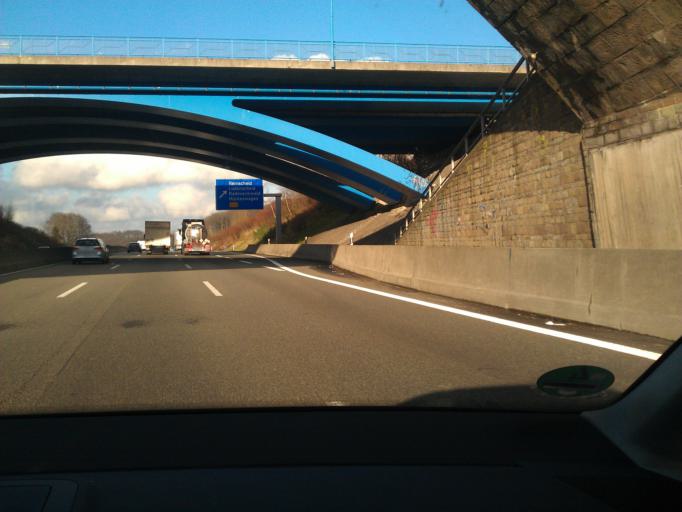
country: DE
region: North Rhine-Westphalia
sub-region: Regierungsbezirk Dusseldorf
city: Remscheid
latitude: 51.1800
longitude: 7.2376
